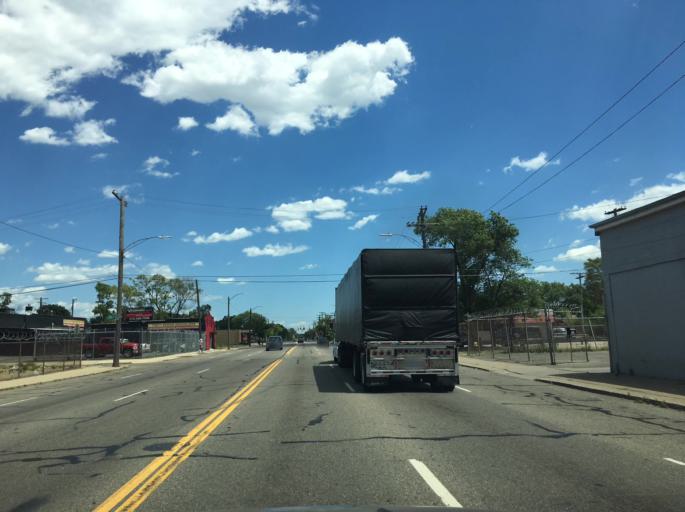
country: US
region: Michigan
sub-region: Wayne County
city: Hamtramck
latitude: 42.4177
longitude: -83.0559
